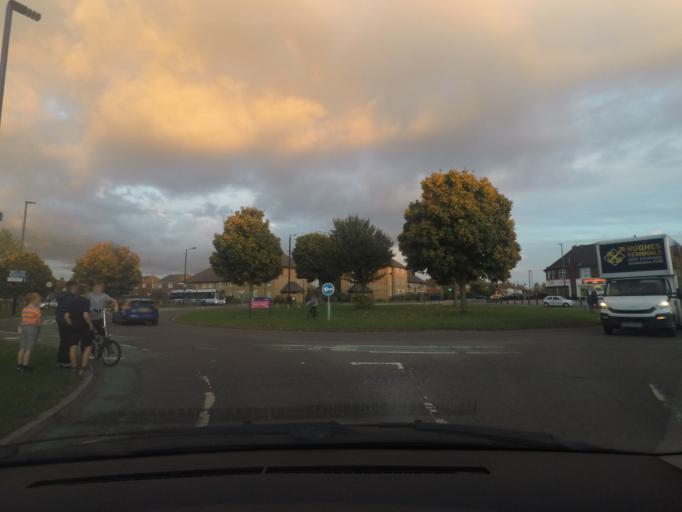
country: GB
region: England
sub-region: City of York
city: York
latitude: 53.9766
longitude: -1.0905
